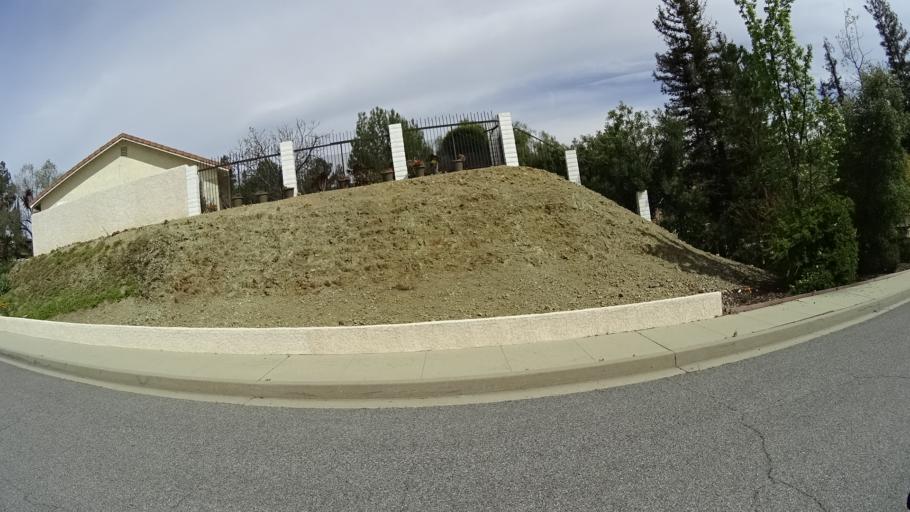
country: US
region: California
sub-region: Ventura County
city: Thousand Oaks
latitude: 34.1479
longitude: -118.8507
